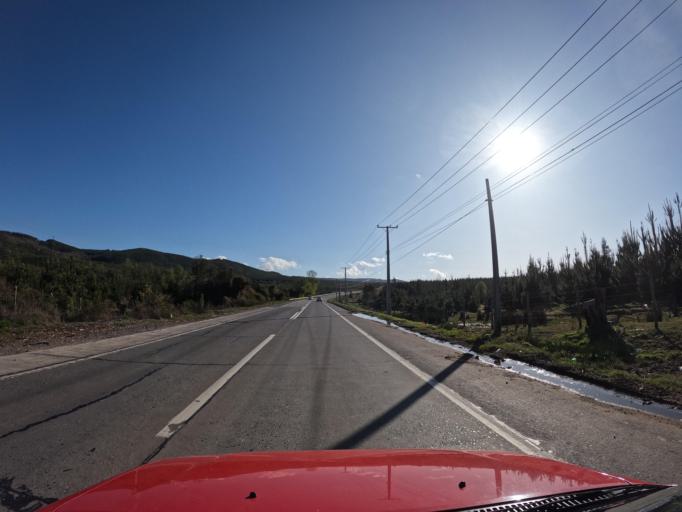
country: CL
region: Maule
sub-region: Provincia de Talca
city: Constitucion
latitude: -35.4462
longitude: -72.3107
